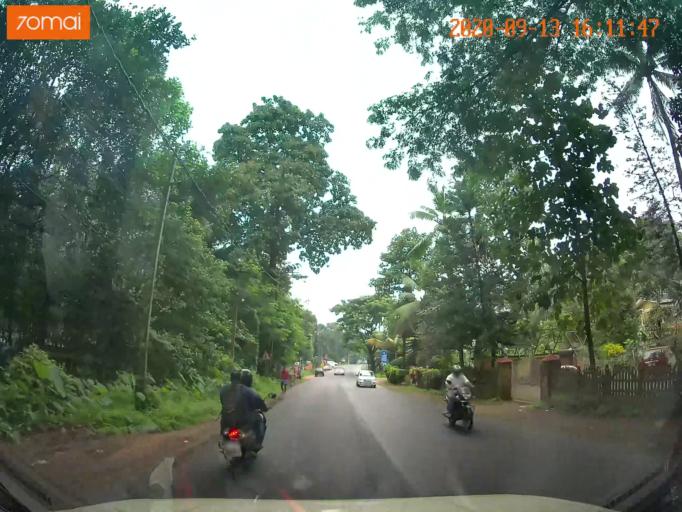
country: IN
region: Kerala
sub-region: Kottayam
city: Palackattumala
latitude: 9.6858
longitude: 76.6140
